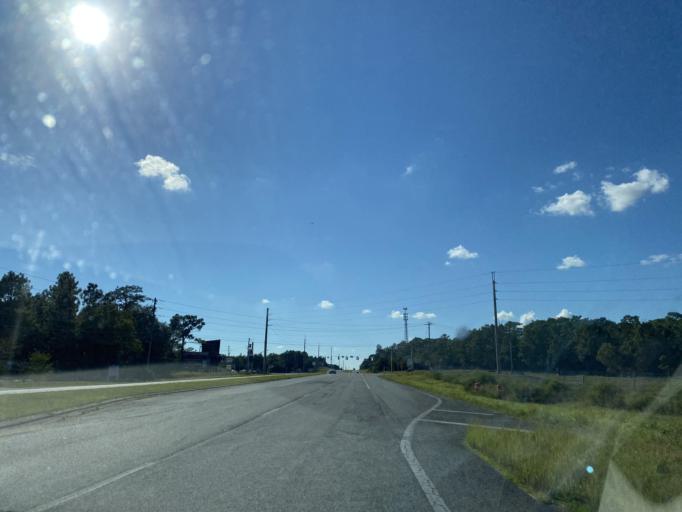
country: US
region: Florida
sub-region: Marion County
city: Dunnellon
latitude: 29.0537
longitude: -82.2813
